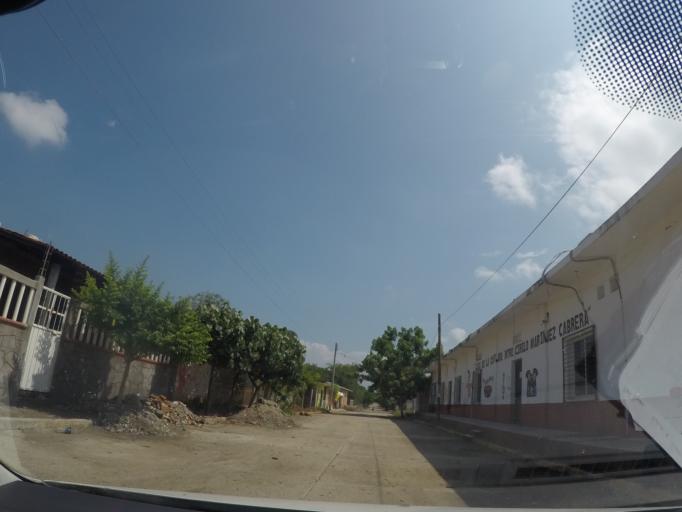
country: MX
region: Oaxaca
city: San Francisco Ixhuatan
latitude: 16.3986
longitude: -94.4602
